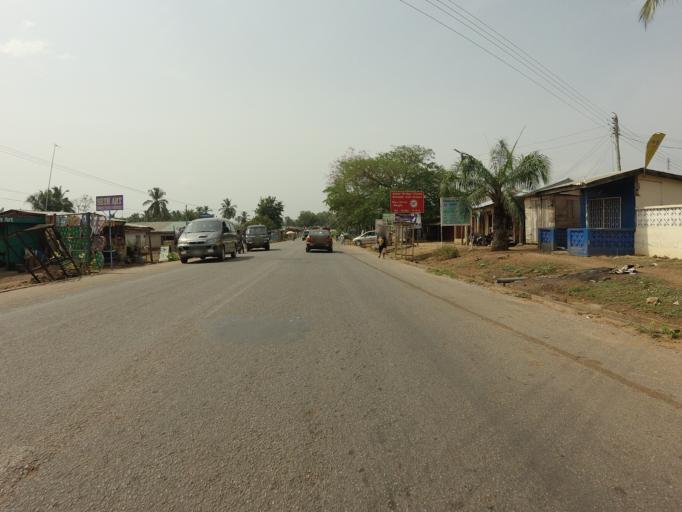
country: GH
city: Akropong
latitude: 6.2467
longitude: 0.1276
